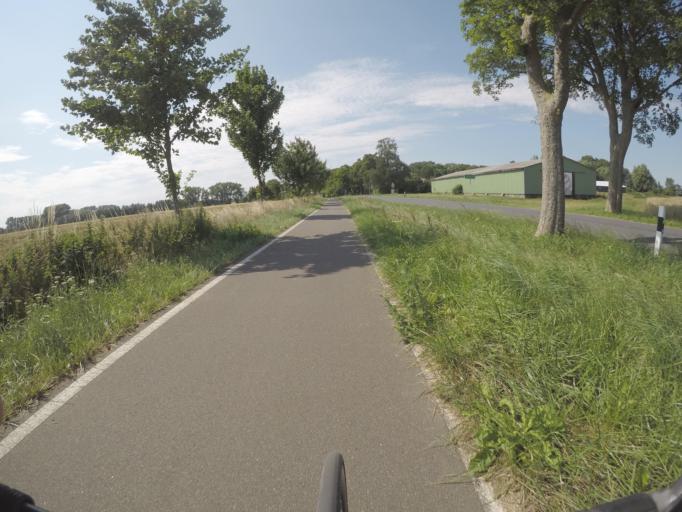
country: DE
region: Mecklenburg-Vorpommern
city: Gingst
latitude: 54.4455
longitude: 13.2042
